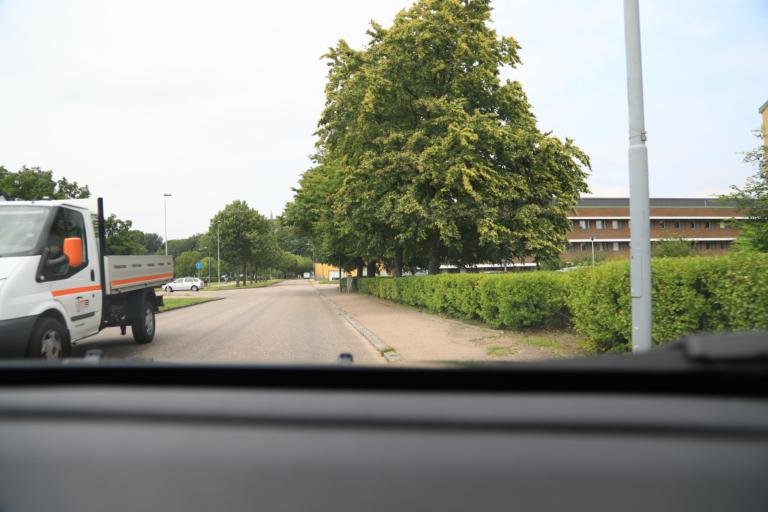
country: SE
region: Halland
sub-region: Halmstads Kommun
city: Halmstad
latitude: 56.6692
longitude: 12.8559
